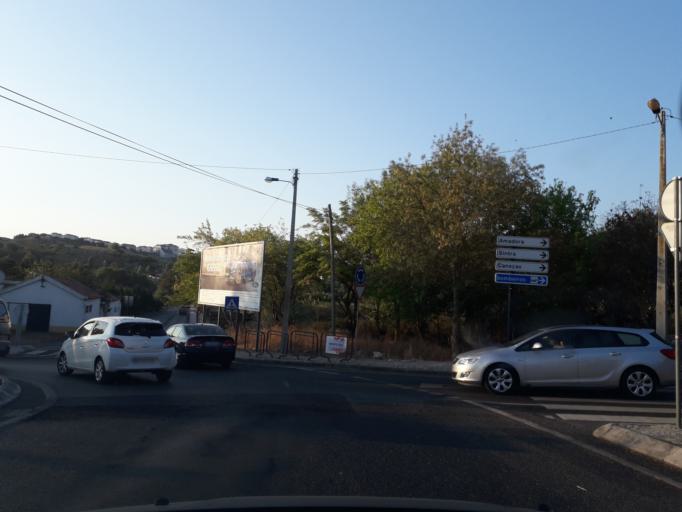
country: PT
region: Lisbon
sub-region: Odivelas
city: Pontinha
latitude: 38.7762
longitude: -9.2057
